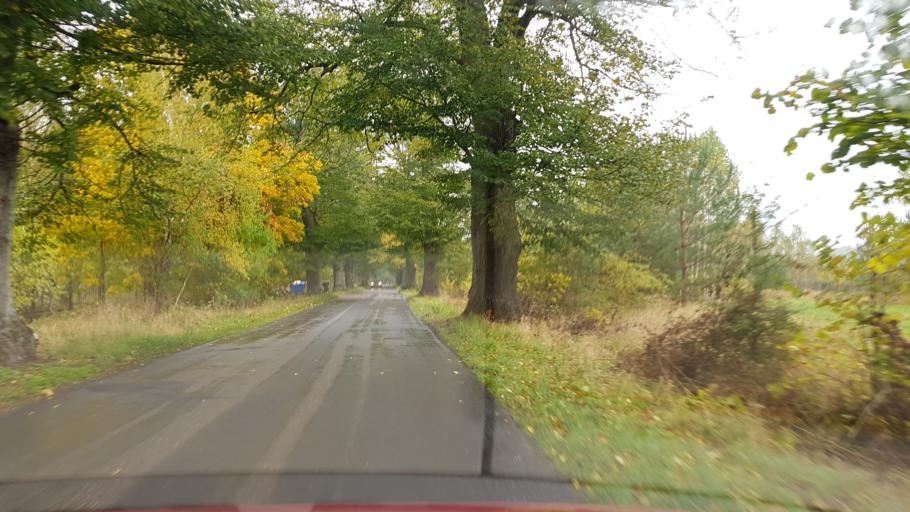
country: PL
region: West Pomeranian Voivodeship
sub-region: Powiat walecki
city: Walcz
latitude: 53.3692
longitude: 16.5075
